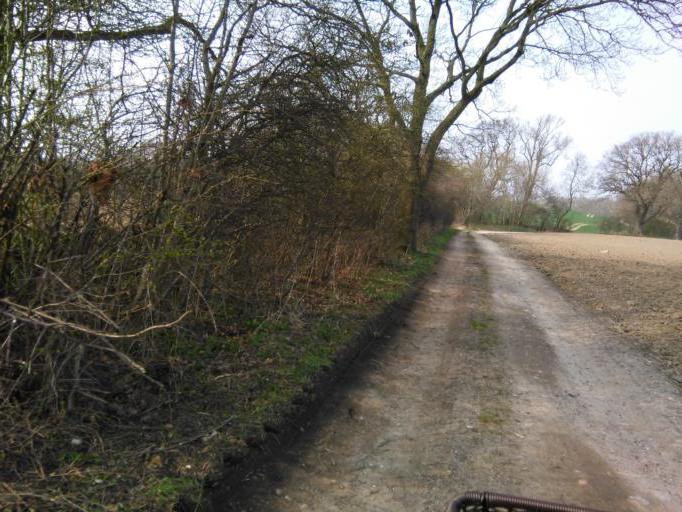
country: DK
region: Central Jutland
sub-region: Arhus Kommune
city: Beder
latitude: 56.0789
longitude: 10.2219
